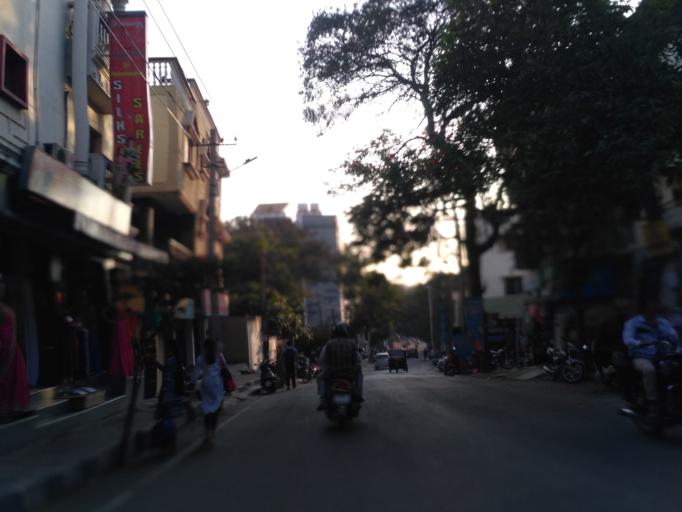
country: IN
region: Karnataka
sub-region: Bangalore Urban
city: Bangalore
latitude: 12.9601
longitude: 77.5369
